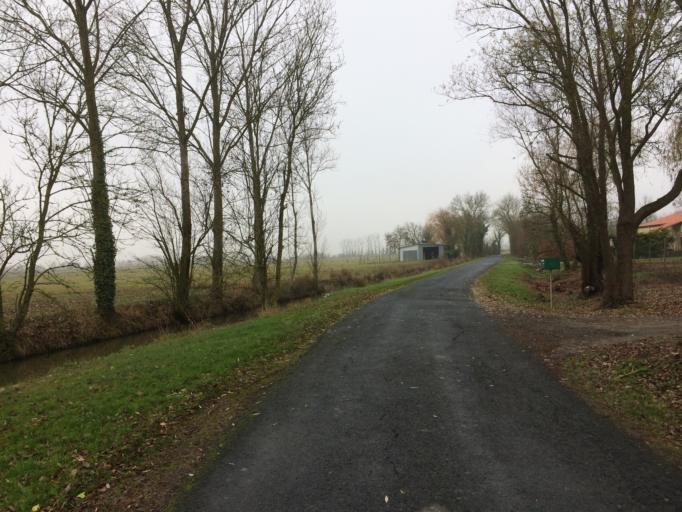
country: FR
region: Pays de la Loire
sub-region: Departement de la Vendee
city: Chaille-les-Marais
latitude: 46.3795
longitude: -1.0247
